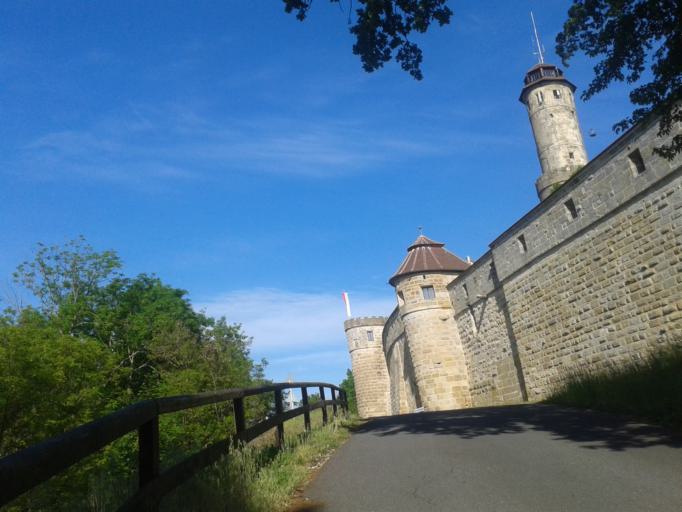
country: DE
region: Bavaria
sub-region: Upper Franconia
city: Stegaurach
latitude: 49.8803
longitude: 10.8701
